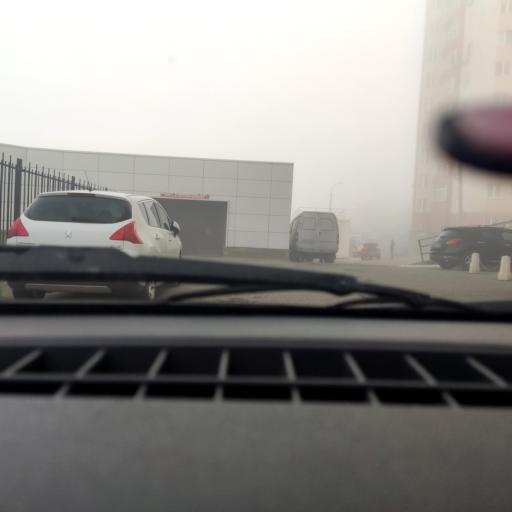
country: RU
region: Bashkortostan
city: Ufa
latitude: 54.7467
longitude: 55.9536
